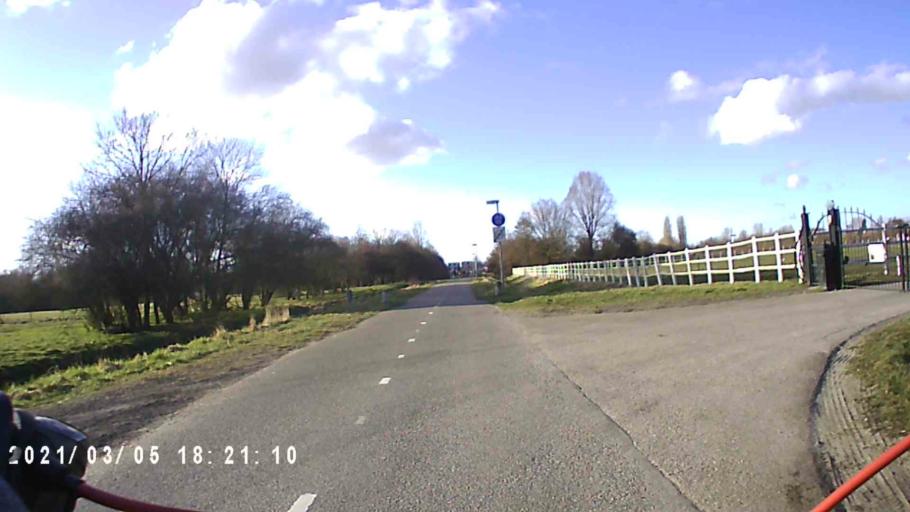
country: NL
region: Groningen
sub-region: Gemeente Groningen
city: Oosterpark
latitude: 53.2384
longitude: 6.5854
